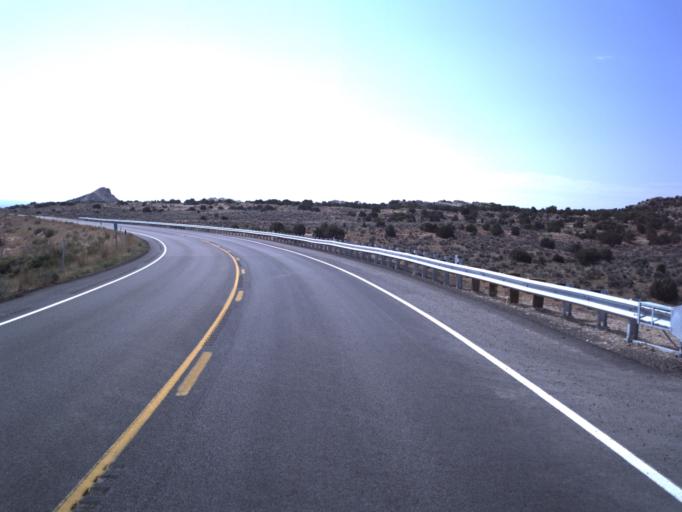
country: US
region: Utah
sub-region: Uintah County
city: Naples
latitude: 40.3569
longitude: -109.4980
